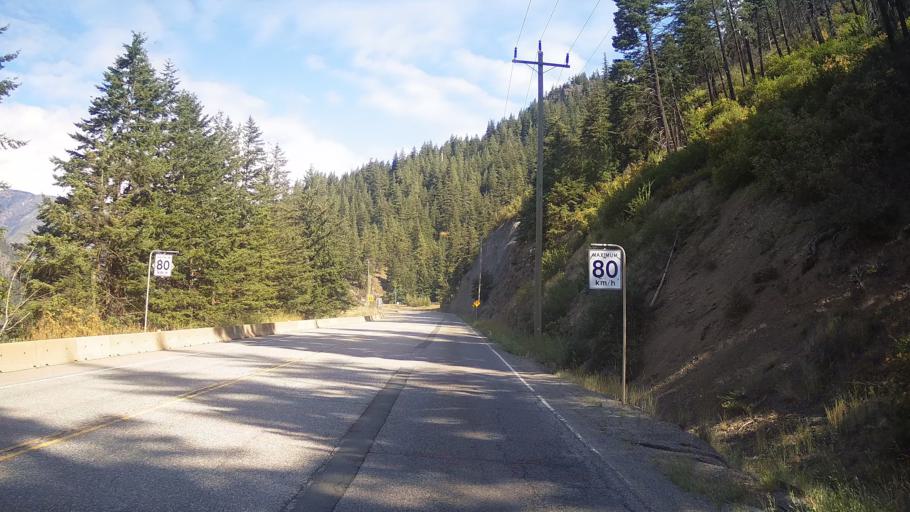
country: CA
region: British Columbia
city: Hope
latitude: 50.0729
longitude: -121.5469
